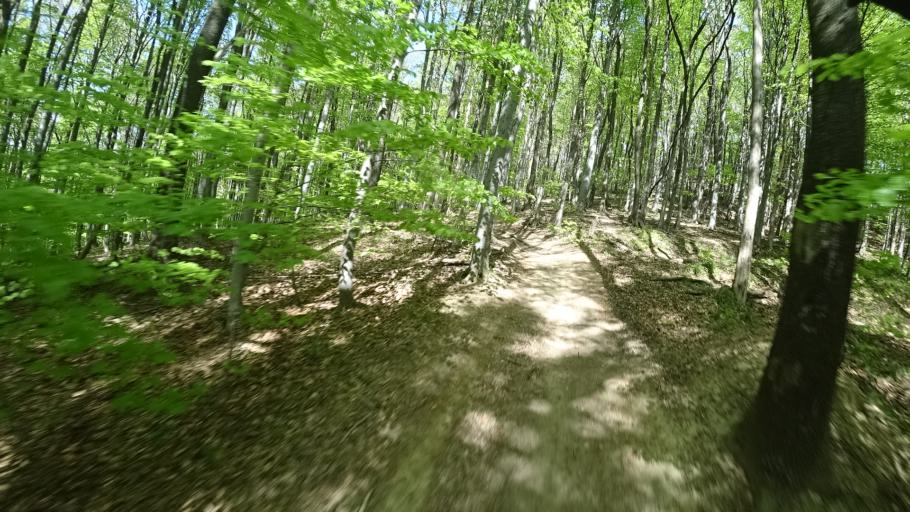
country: HR
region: Zagrebacka
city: Jablanovec
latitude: 45.8795
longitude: 15.9067
